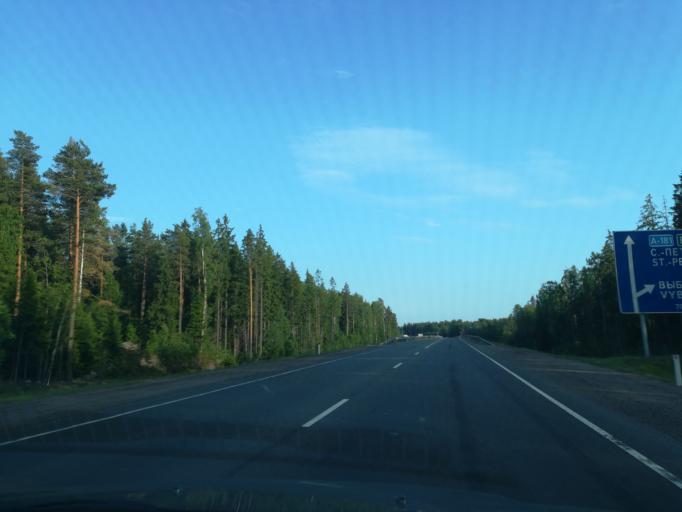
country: RU
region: Leningrad
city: Vyborg
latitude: 60.6837
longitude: 28.8650
